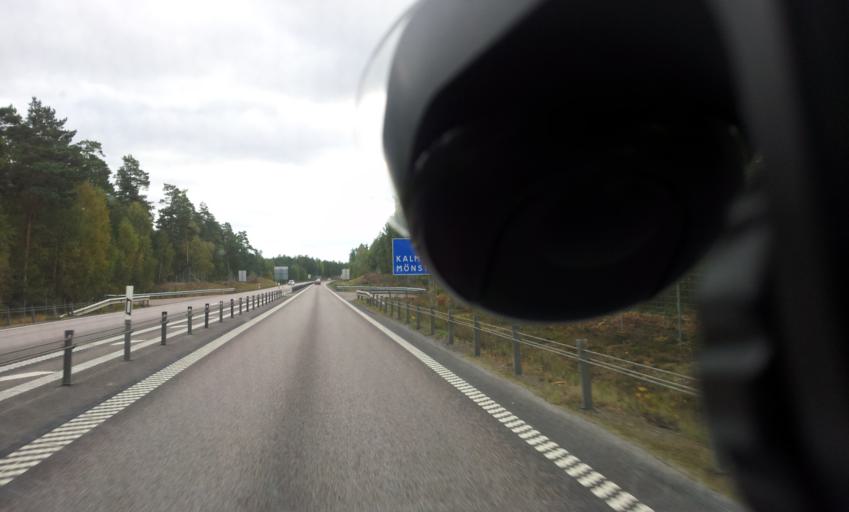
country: SE
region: Kalmar
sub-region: Oskarshamns Kommun
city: Oskarshamn
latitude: 57.2453
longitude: 16.4272
